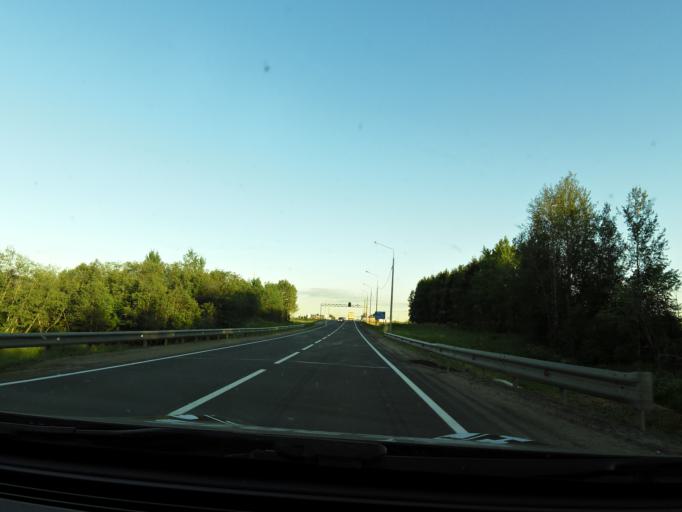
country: RU
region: Vologda
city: Gryazovets
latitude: 58.7471
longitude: 40.2864
